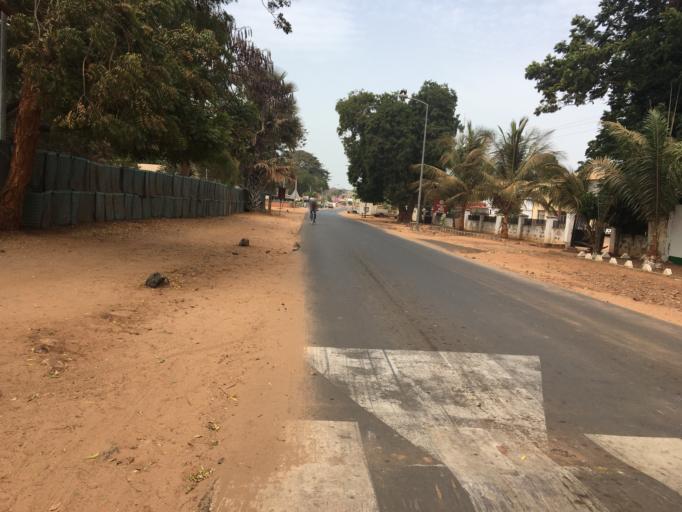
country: GM
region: Banjul
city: Bakau
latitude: 13.4797
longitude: -16.6800
